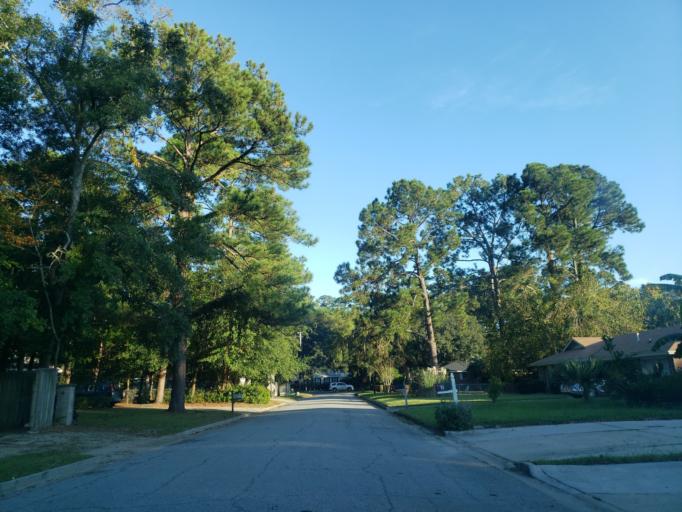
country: US
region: Georgia
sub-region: Chatham County
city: Isle of Hope
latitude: 31.9959
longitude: -81.0646
